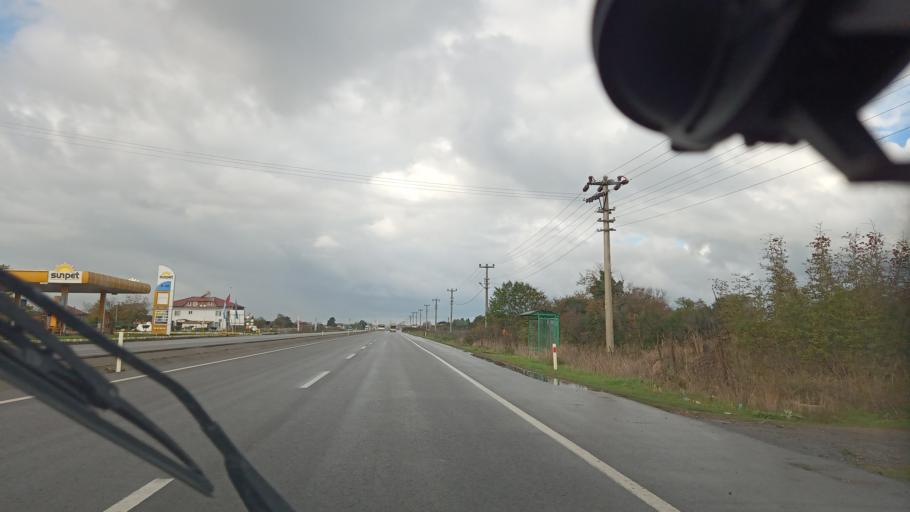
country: TR
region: Sakarya
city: Karasu
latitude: 41.0804
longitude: 30.7691
